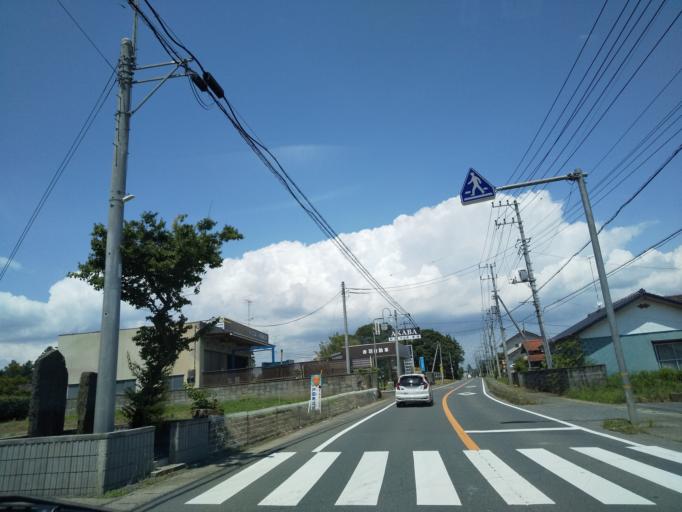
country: JP
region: Ibaraki
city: Ishioka
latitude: 36.1858
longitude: 140.3707
